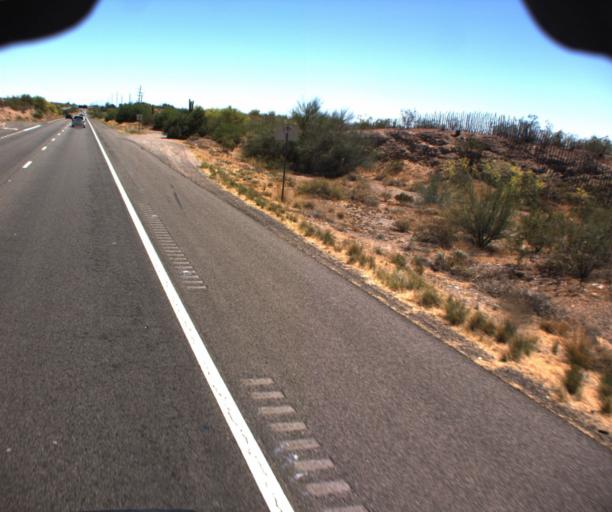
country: US
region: Arizona
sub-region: Maricopa County
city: Wickenburg
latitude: 33.8768
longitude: -112.6495
